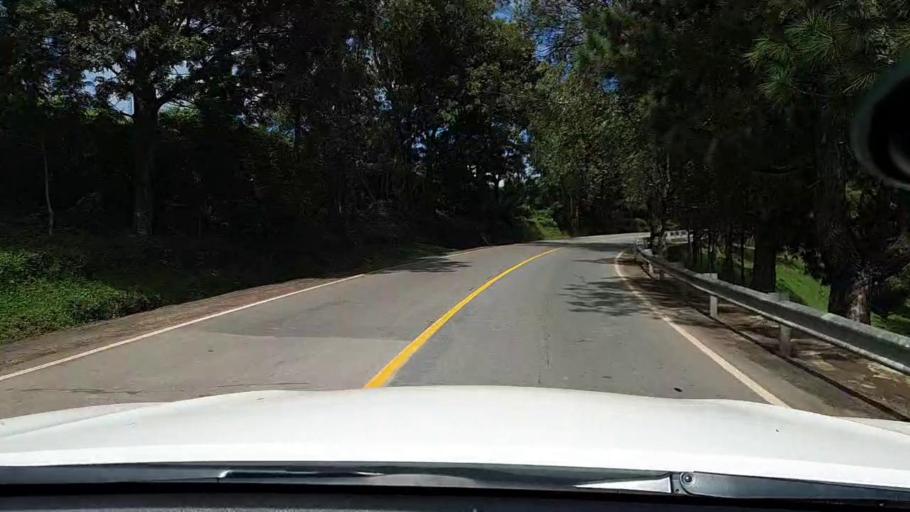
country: RW
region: Kigali
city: Kigali
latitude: -1.8237
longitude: 29.9432
